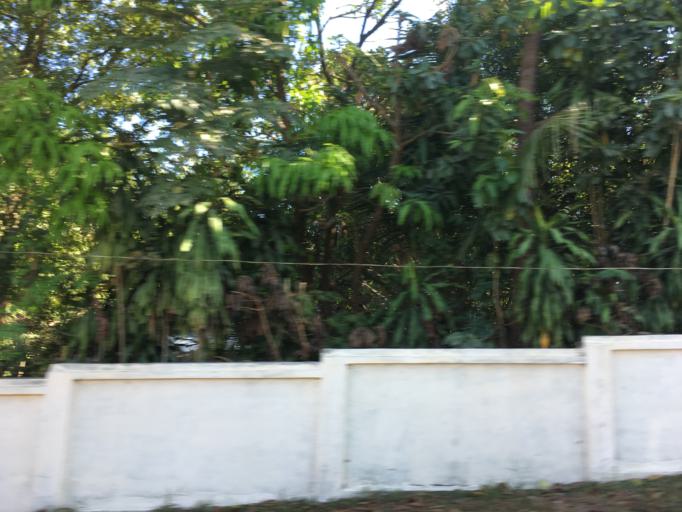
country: MM
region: Mon
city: Mawlamyine
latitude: 16.4849
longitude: 97.6277
